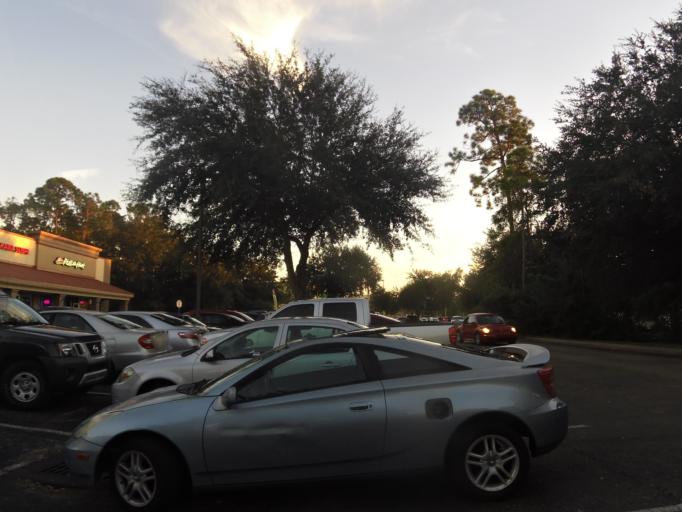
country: US
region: Florida
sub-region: Flagler County
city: Palm Coast
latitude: 29.5529
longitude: -81.2359
